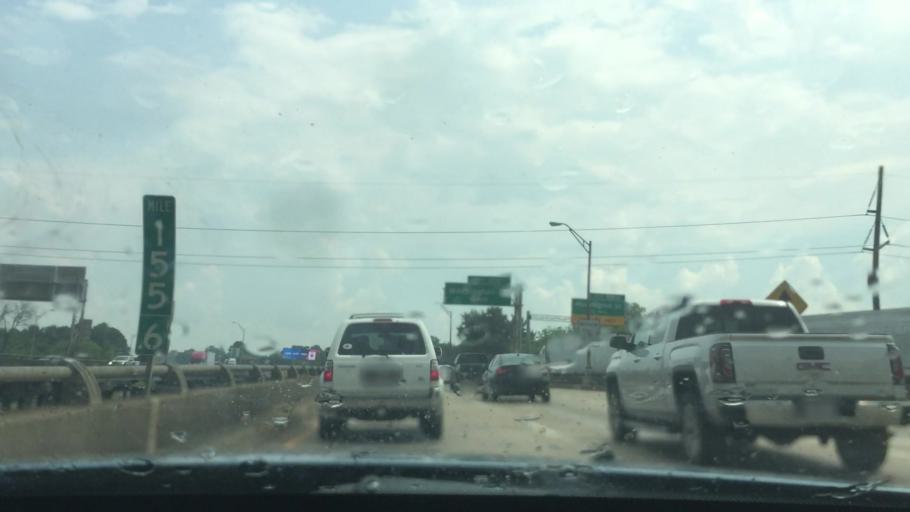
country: US
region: Louisiana
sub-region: East Baton Rouge Parish
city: Baton Rouge
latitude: 30.4380
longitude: -91.1783
